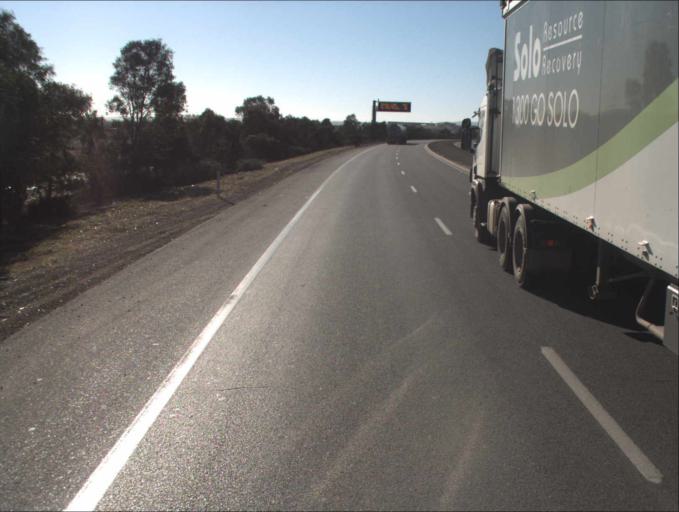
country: AU
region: South Australia
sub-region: Port Adelaide Enfield
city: Alberton
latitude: -34.8355
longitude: 138.5286
